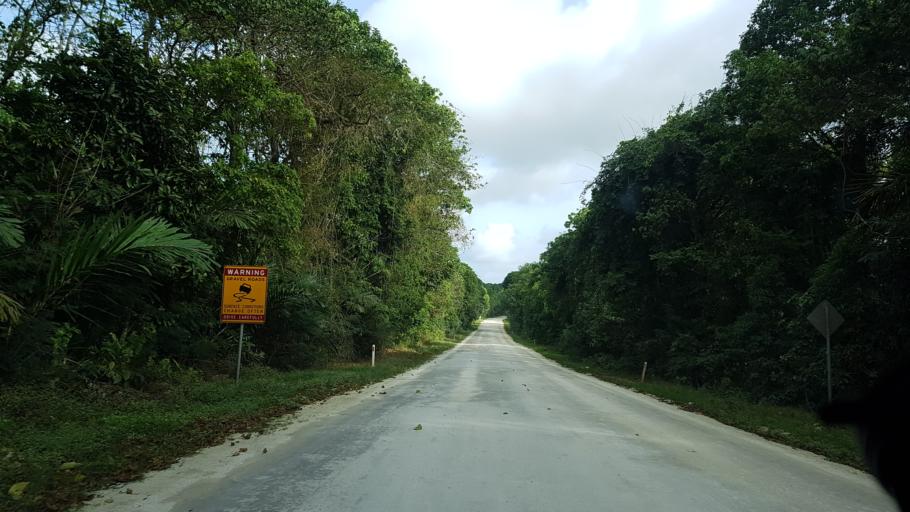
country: CX
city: Flying Fish Cove
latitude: -10.4537
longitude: 105.6880
